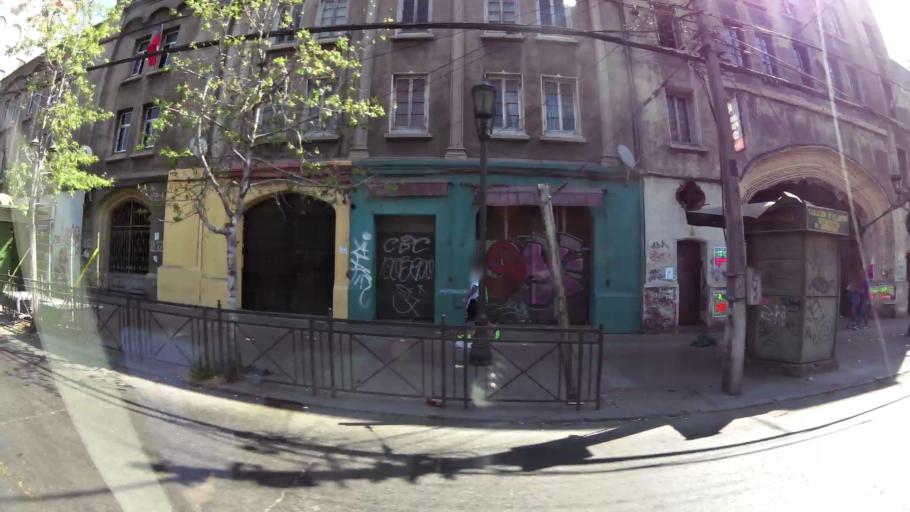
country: CL
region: Santiago Metropolitan
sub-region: Provincia de Santiago
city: Santiago
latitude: -33.4296
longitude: -70.6536
